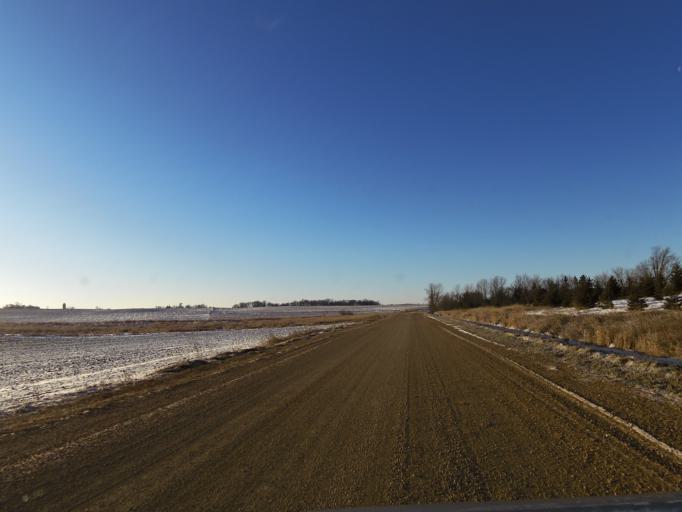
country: US
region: Minnesota
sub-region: Scott County
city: Jordan
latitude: 44.6770
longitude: -93.5365
